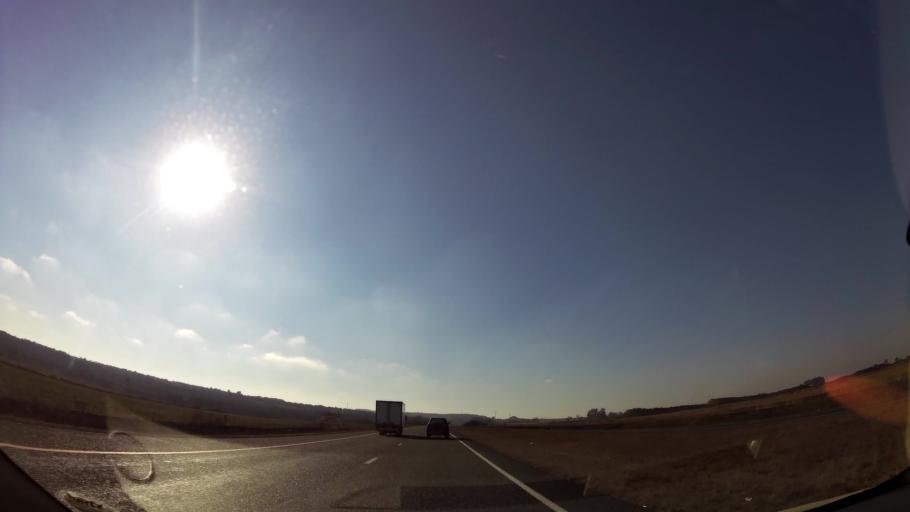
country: ZA
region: Gauteng
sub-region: City of Tshwane Metropolitan Municipality
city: Bronkhorstspruit
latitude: -26.0175
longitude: 28.9411
